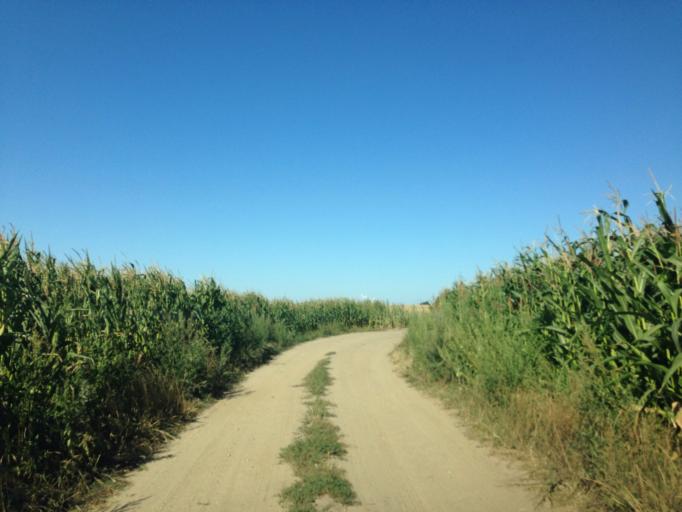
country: PL
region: Kujawsko-Pomorskie
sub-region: Powiat brodnicki
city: Brodnica
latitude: 53.2119
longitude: 19.4129
